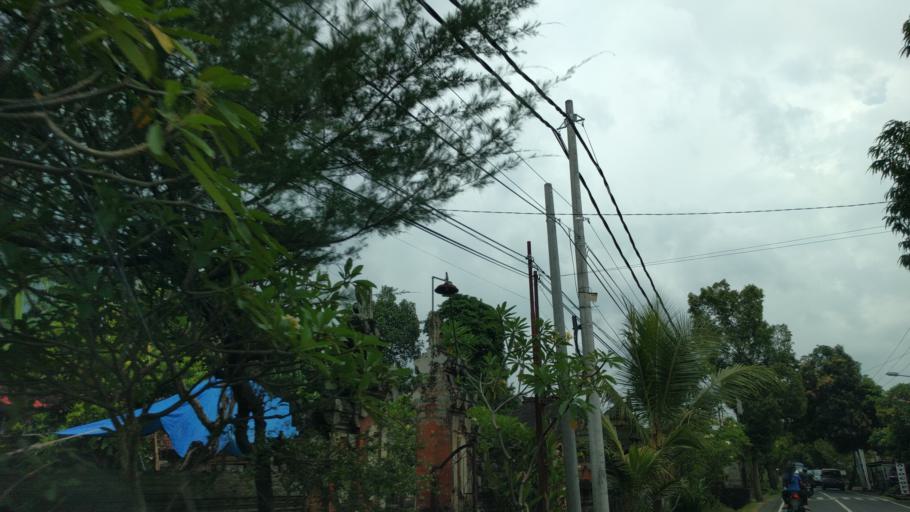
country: ID
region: Bali
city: Banjar Pande
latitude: -8.5105
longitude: 115.2413
